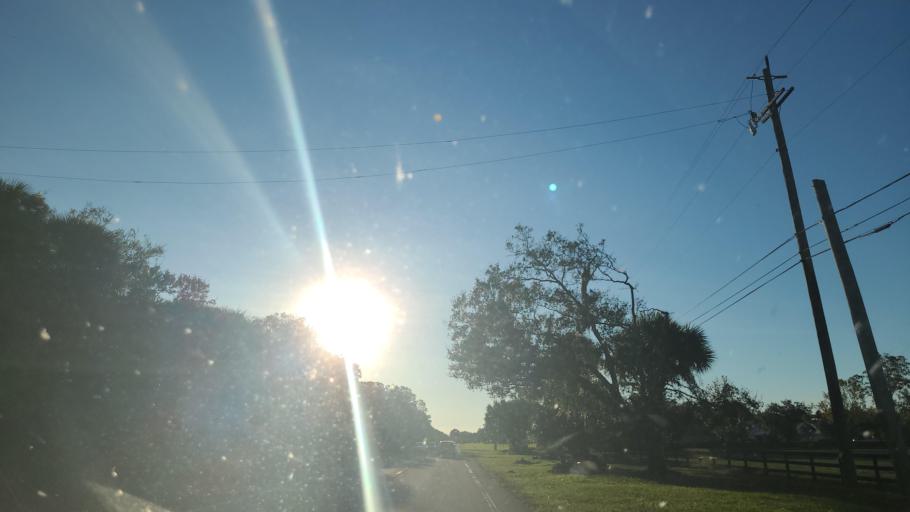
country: US
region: Florida
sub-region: Indian River County
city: Vero Beach South
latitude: 27.6091
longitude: -80.4361
